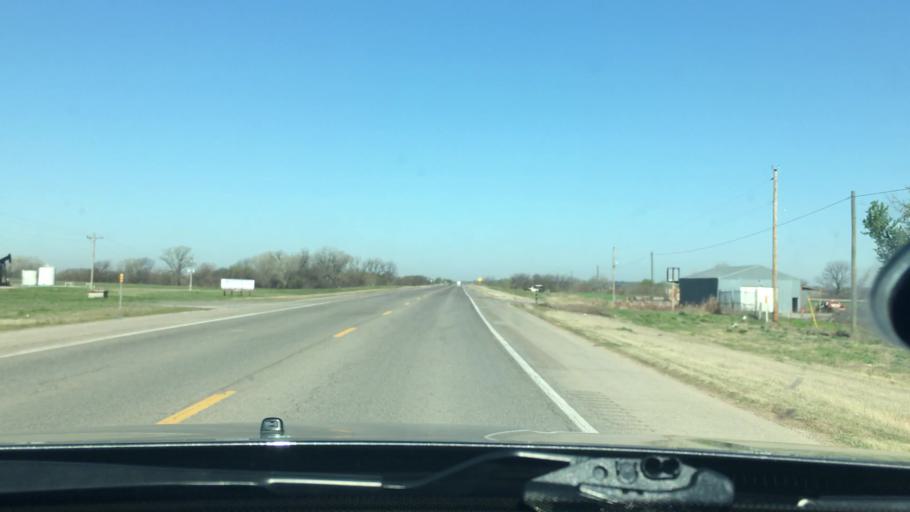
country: US
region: Oklahoma
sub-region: Garvin County
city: Lindsay
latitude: 34.8288
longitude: -97.5677
